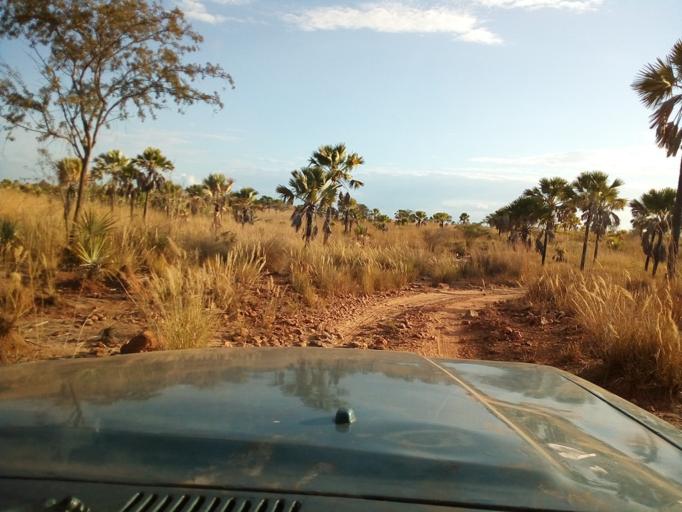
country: MG
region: Boeny
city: Sitampiky
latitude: -16.1240
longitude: 45.5331
